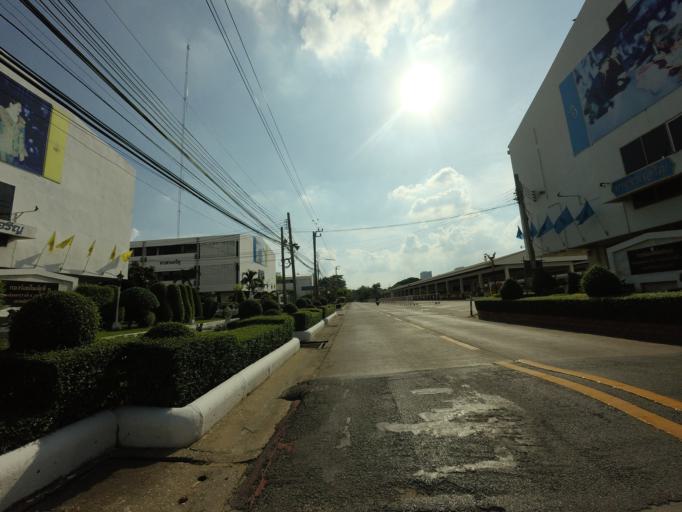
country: TH
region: Bangkok
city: Din Daeng
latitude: 13.7785
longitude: 100.5515
